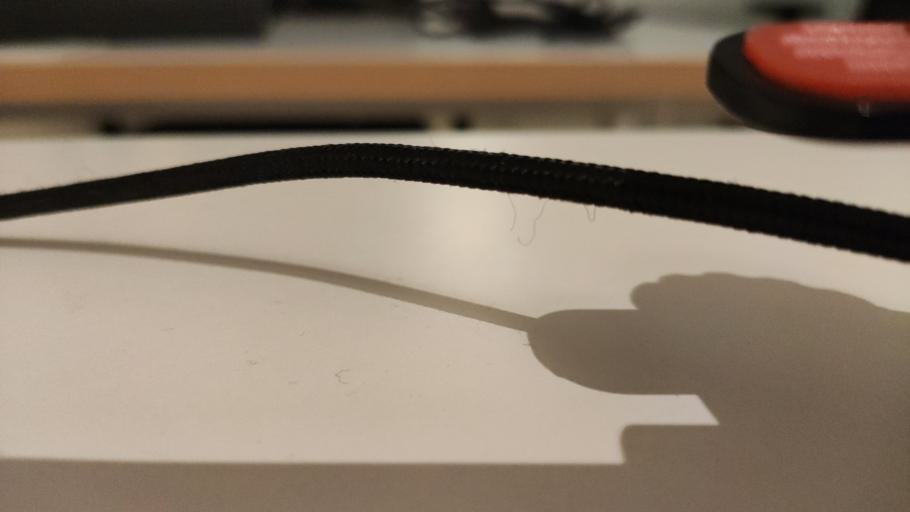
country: RU
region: Moskovskaya
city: Orekhovo-Zuyevo
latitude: 55.8313
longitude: 38.9652
